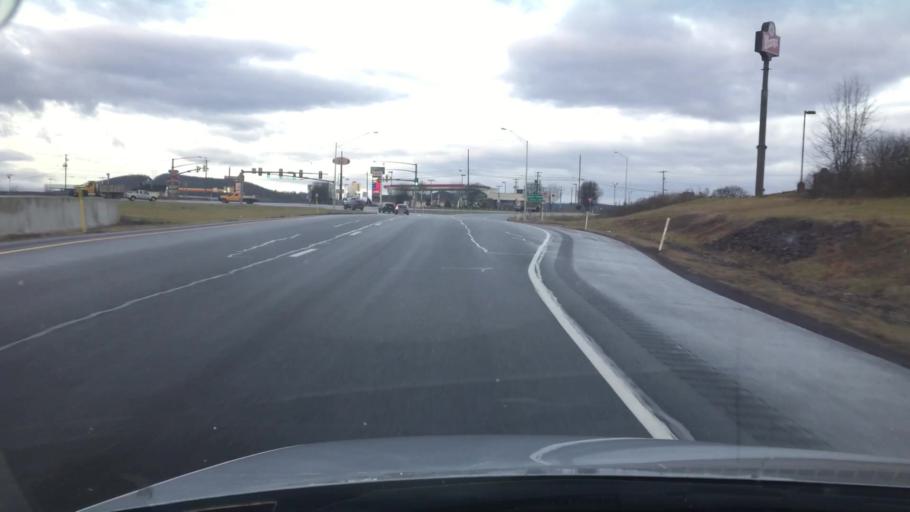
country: US
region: Pennsylvania
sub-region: Columbia County
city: Bloomsburg
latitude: 41.0148
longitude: -76.4892
